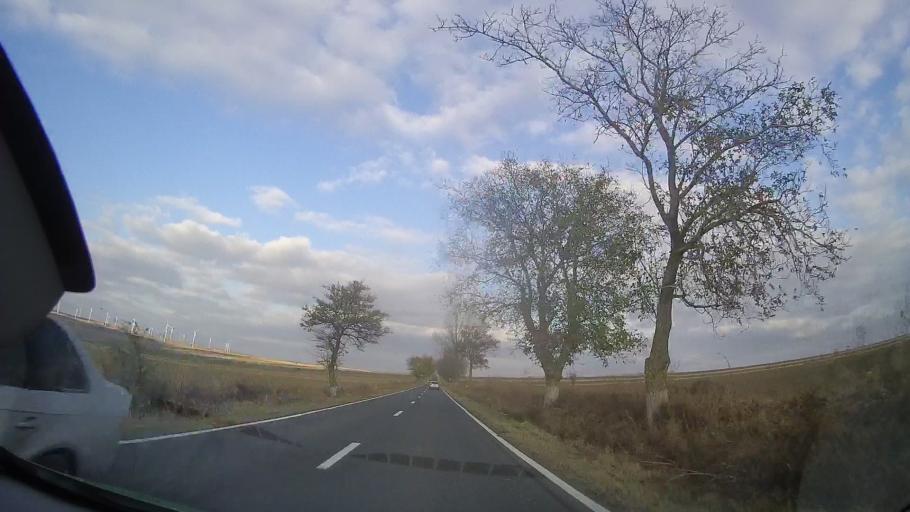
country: RO
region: Tulcea
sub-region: Comuna Topolog
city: Topolog
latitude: 44.8582
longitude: 28.3403
